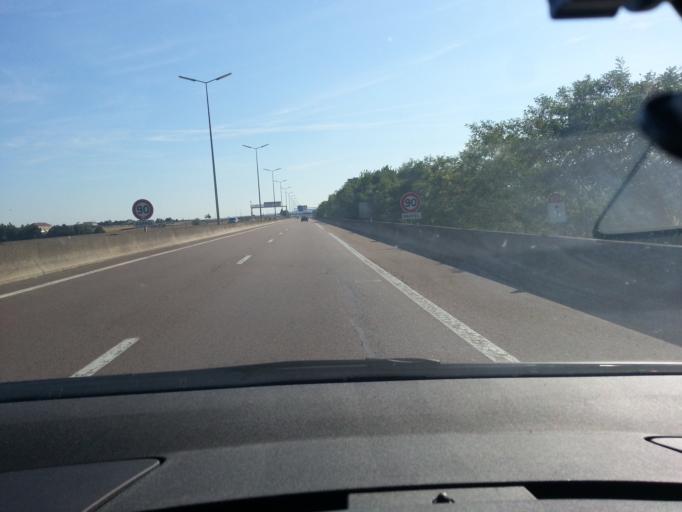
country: FR
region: Bourgogne
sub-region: Departement de la Cote-d'Or
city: Longvic
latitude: 47.2809
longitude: 5.0487
